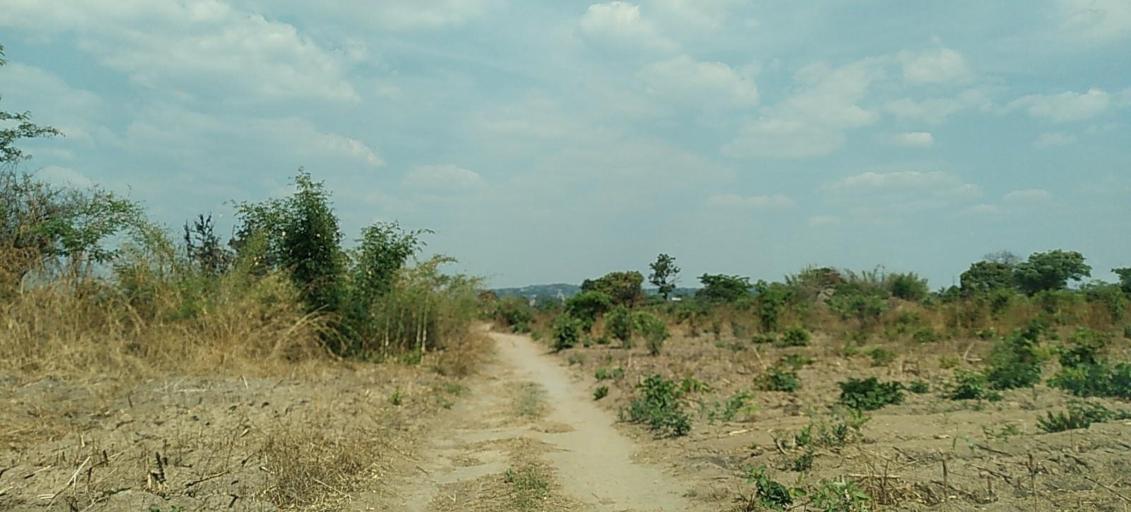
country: ZM
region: Copperbelt
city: Chililabombwe
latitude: -12.3505
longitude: 27.7949
